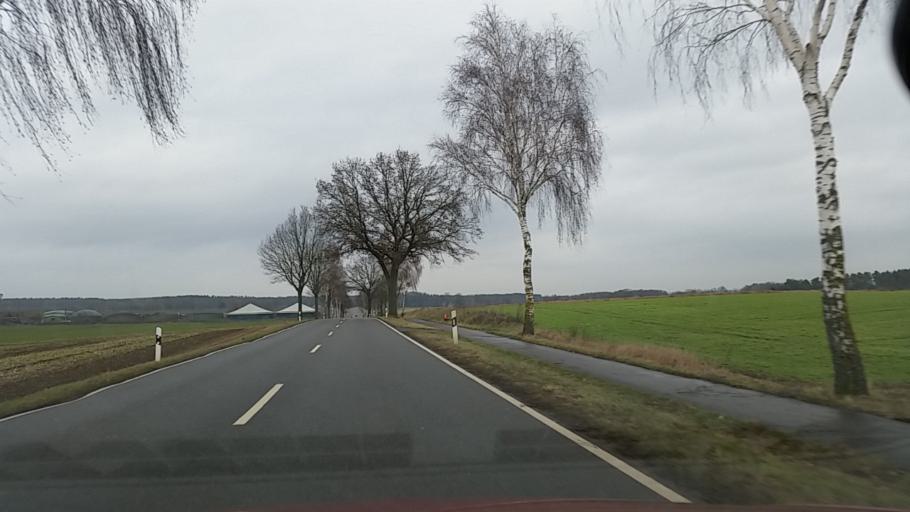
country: DE
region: Lower Saxony
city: Bispingen
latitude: 53.1159
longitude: 10.0007
